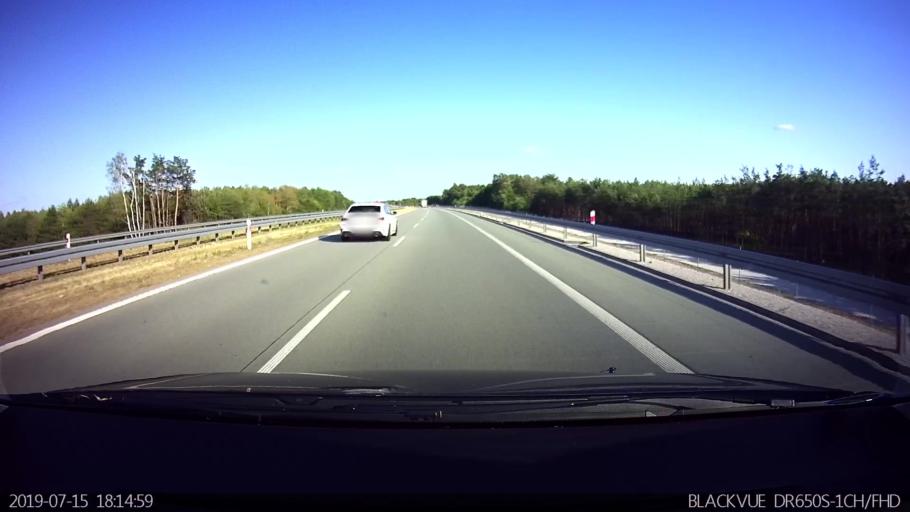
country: PL
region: Lodz Voivodeship
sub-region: Powiat zdunskowolski
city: Zdunska Wola
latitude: 51.5852
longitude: 18.8994
